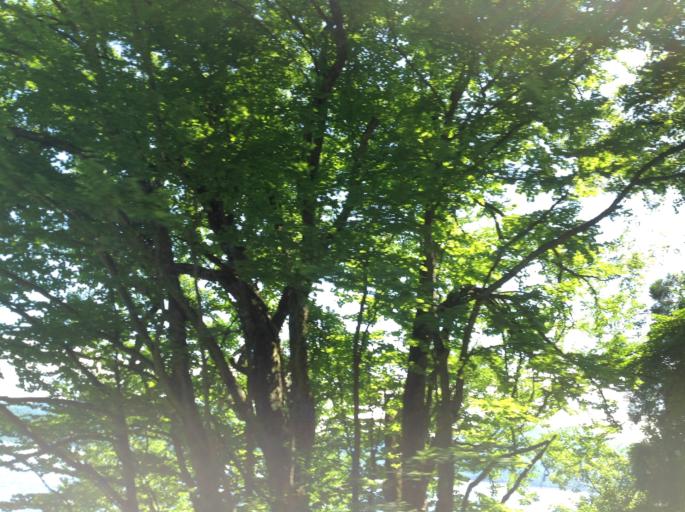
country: JP
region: Akita
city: Kakunodatemachi
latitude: 39.7090
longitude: 140.6377
